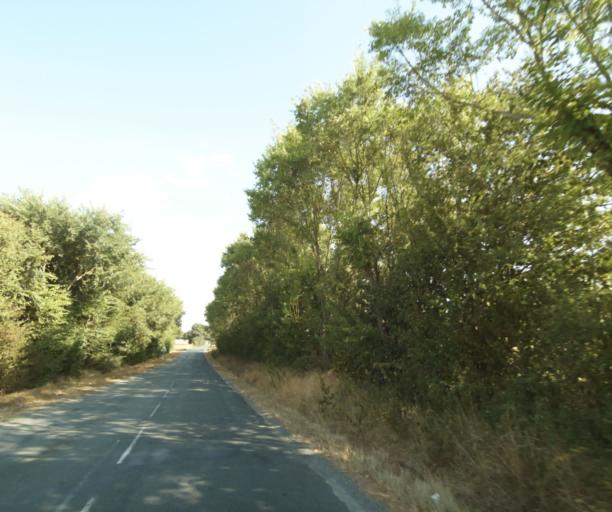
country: FR
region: Poitou-Charentes
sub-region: Departement de la Charente-Maritime
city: Tonnay-Charente
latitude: 45.9616
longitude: -0.8843
